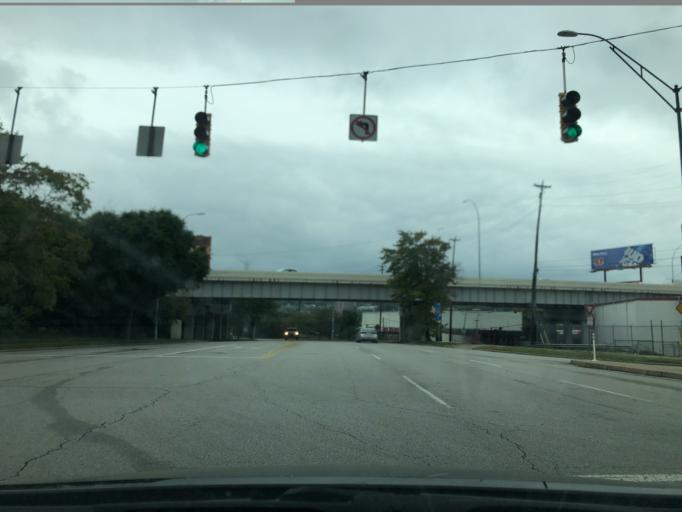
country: US
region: Kentucky
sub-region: Kenton County
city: Ludlow
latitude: 39.1016
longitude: -84.5302
